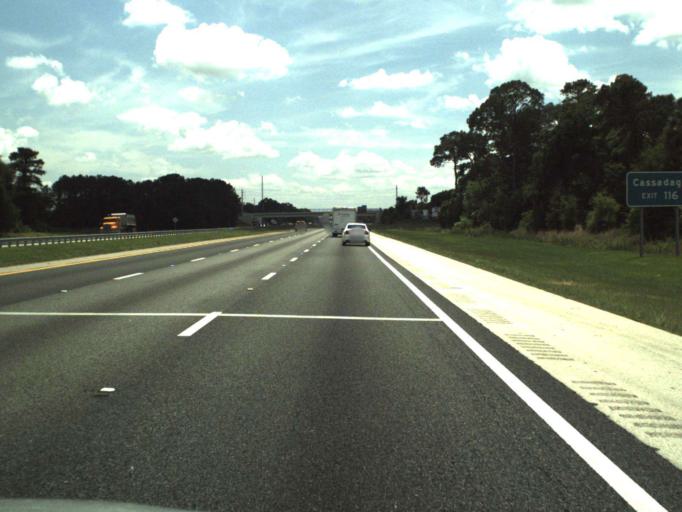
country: US
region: Florida
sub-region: Volusia County
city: Lake Helen
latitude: 28.9906
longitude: -81.2467
